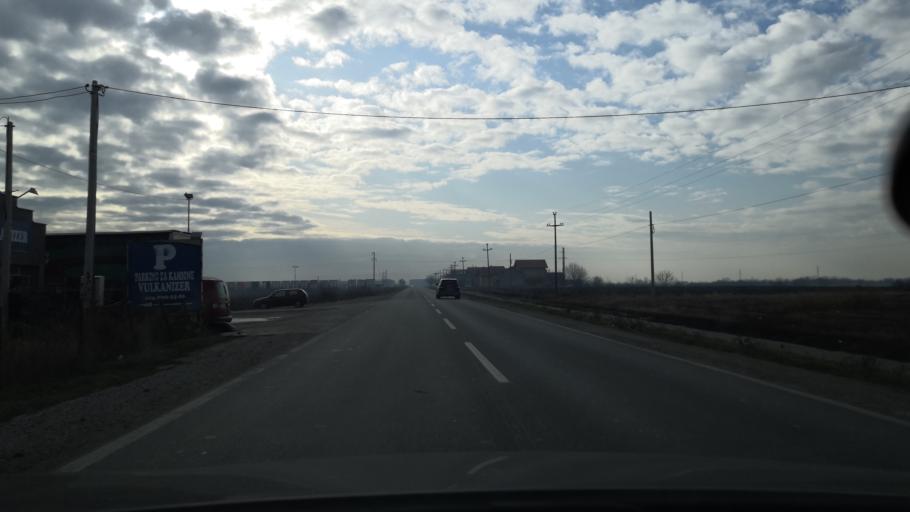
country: RS
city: Ugrinovci
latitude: 44.8637
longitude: 20.2047
